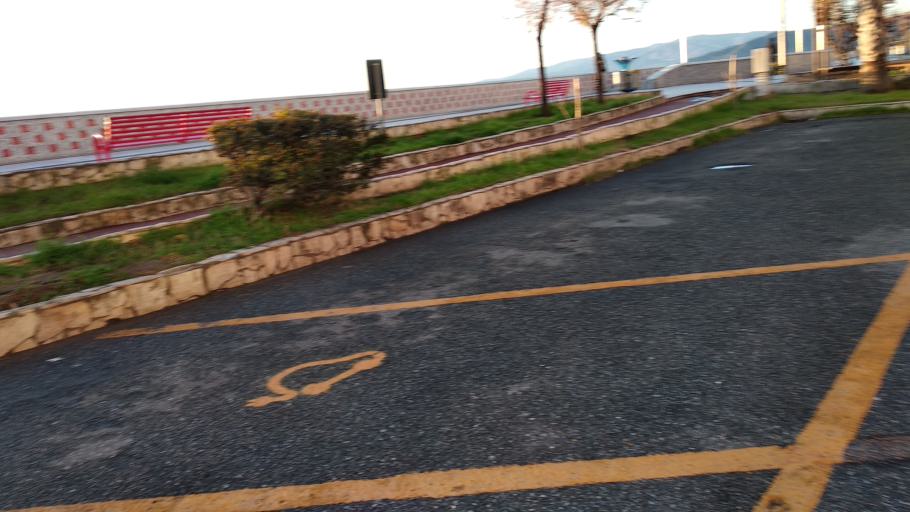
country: IT
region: Calabria
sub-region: Provincia di Catanzaro
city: Roccelletta
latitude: 38.8241
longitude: 16.6214
